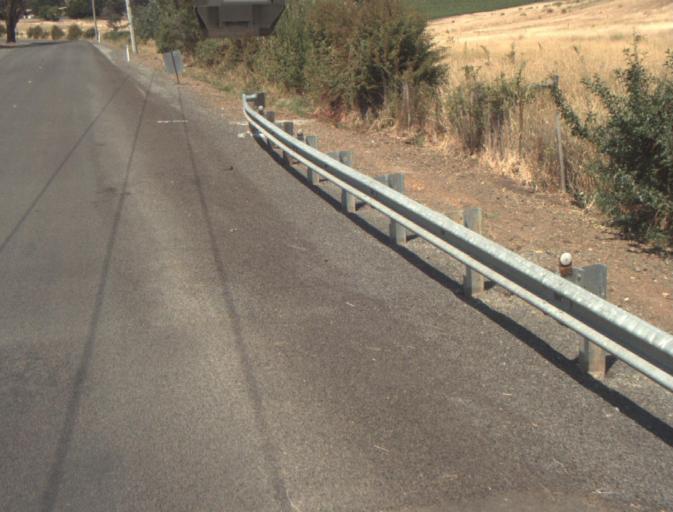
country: AU
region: Tasmania
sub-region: Launceston
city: Summerhill
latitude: -41.4945
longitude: 147.1817
